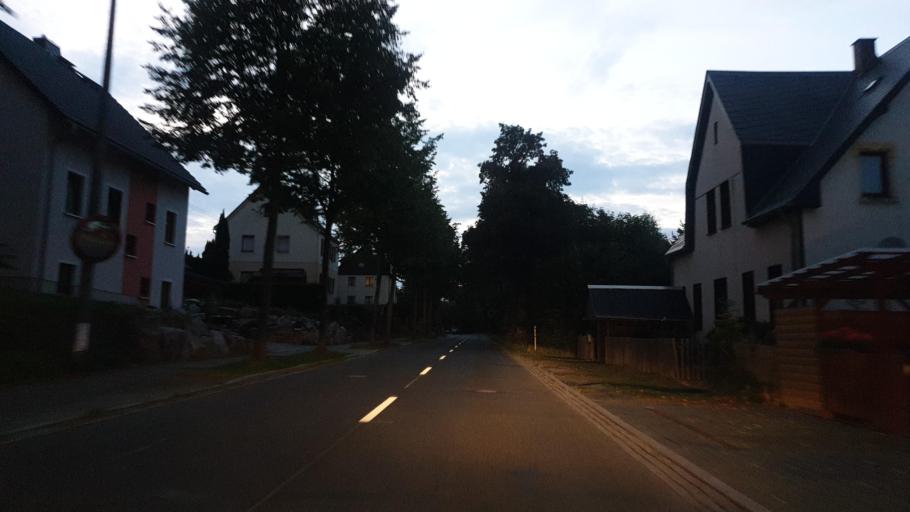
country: DE
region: Saxony
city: Auerbach
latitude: 50.5059
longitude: 12.4285
